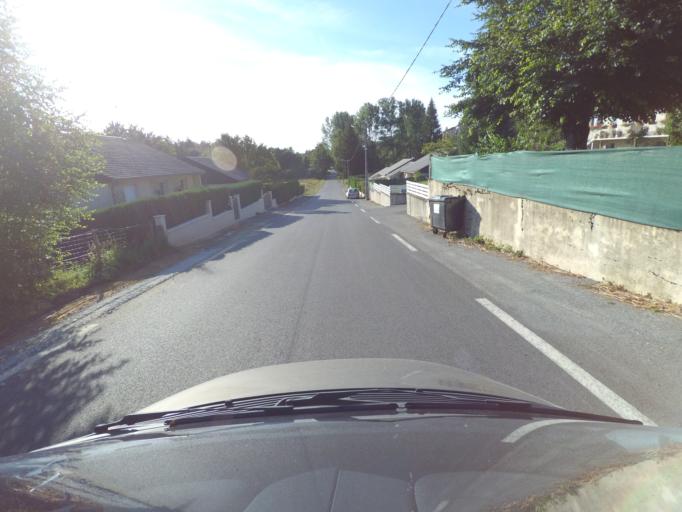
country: FR
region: Limousin
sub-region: Departement de la Correze
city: Bugeat
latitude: 45.7028
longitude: 2.0522
